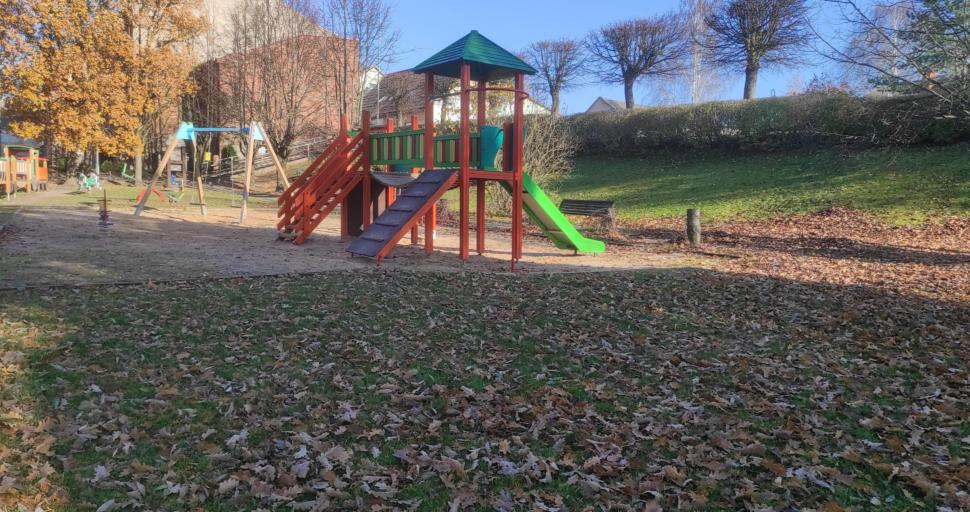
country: LV
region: Saldus Rajons
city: Saldus
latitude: 56.6649
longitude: 22.4914
